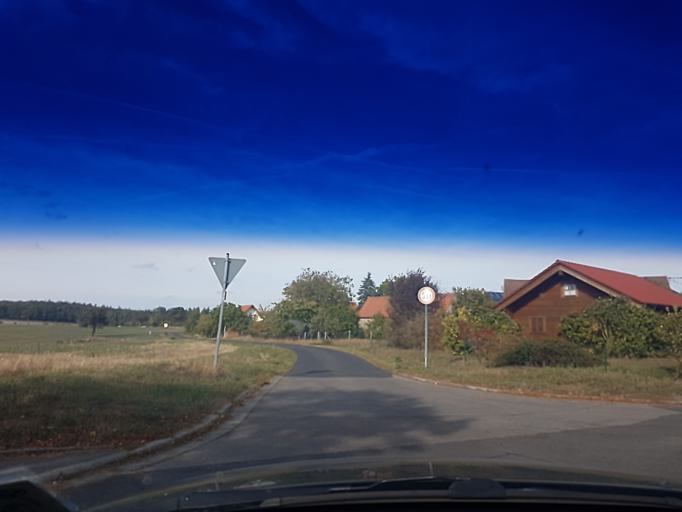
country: DE
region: Bavaria
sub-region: Regierungsbezirk Mittelfranken
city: Burghaslach
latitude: 49.7744
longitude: 10.5431
